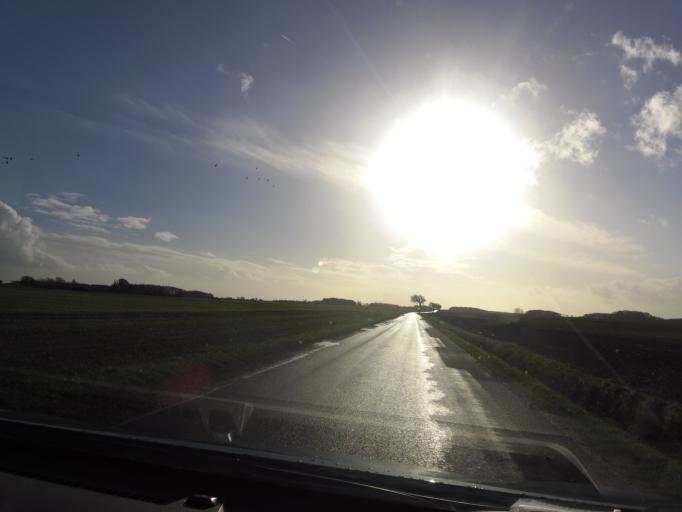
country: DK
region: Central Jutland
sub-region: Odder Kommune
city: Odder
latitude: 55.8841
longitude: 10.1712
